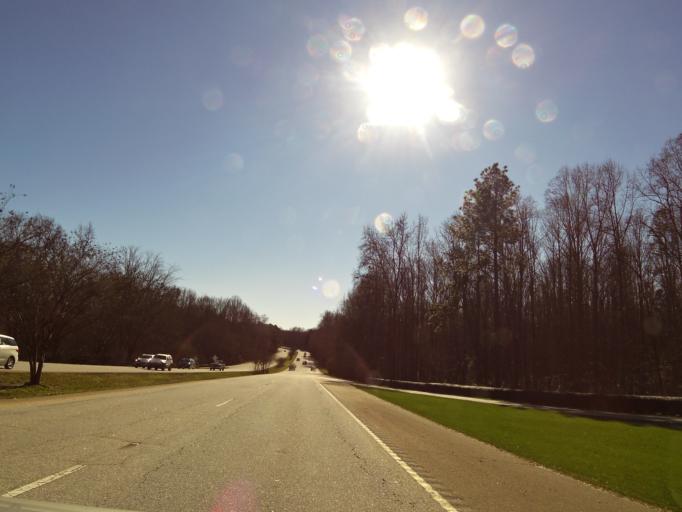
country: US
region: South Carolina
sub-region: Greenville County
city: Travelers Rest
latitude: 34.9243
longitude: -82.4332
